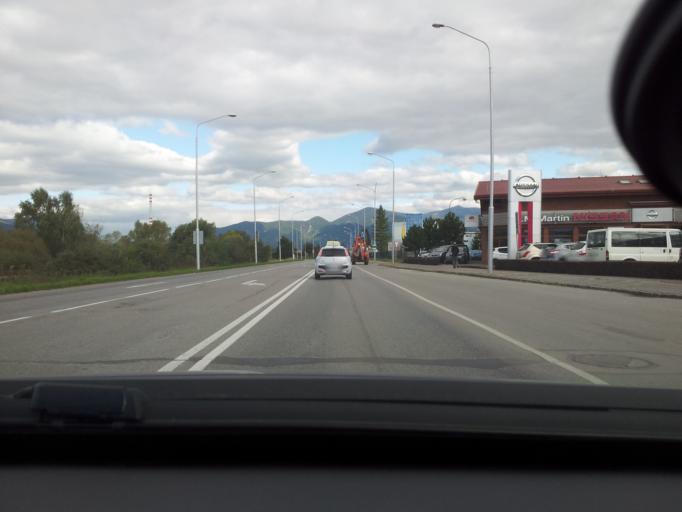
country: SK
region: Zilinsky
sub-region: Okres Martin
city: Martin
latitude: 49.0439
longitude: 18.9103
